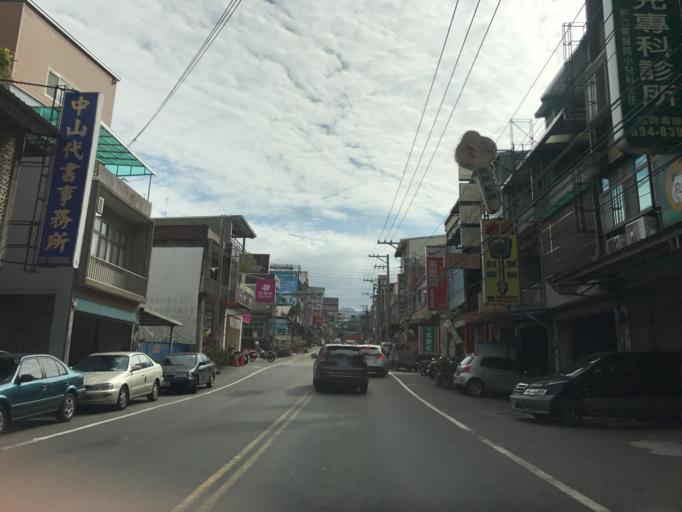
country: TW
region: Taiwan
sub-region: Hsinchu
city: Zhubei
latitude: 24.7210
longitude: 121.0964
